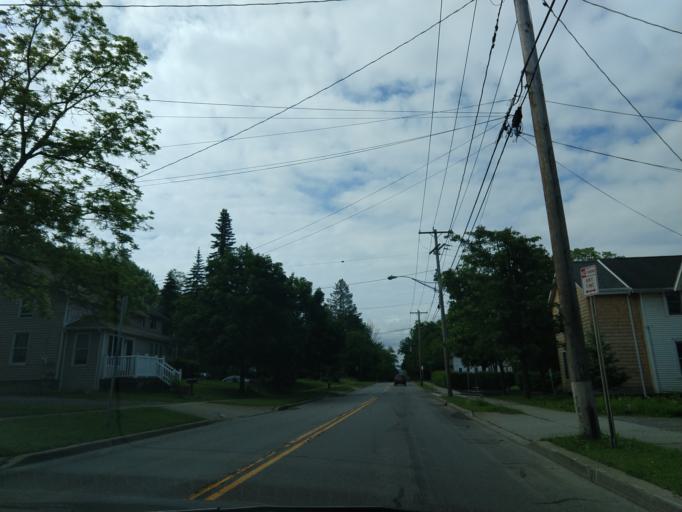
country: US
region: New York
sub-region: Erie County
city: East Aurora
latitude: 42.7639
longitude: -78.6080
